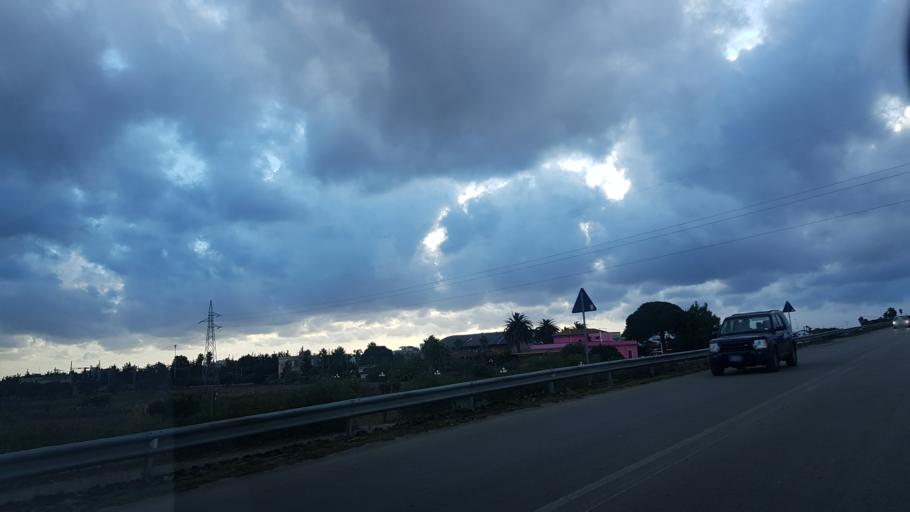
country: IT
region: Apulia
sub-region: Provincia di Brindisi
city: San Pietro Vernotico
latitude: 40.4995
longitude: 17.9996
